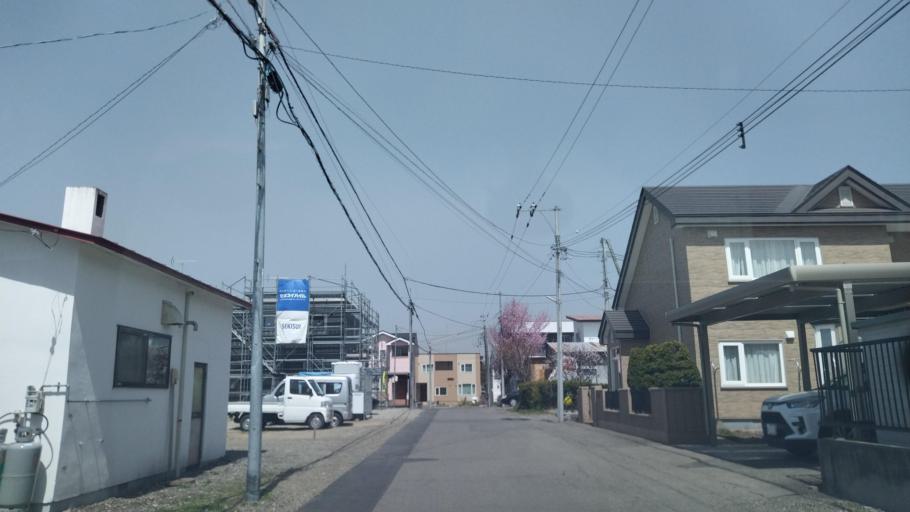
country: JP
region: Hokkaido
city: Obihiro
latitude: 42.9365
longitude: 143.1870
